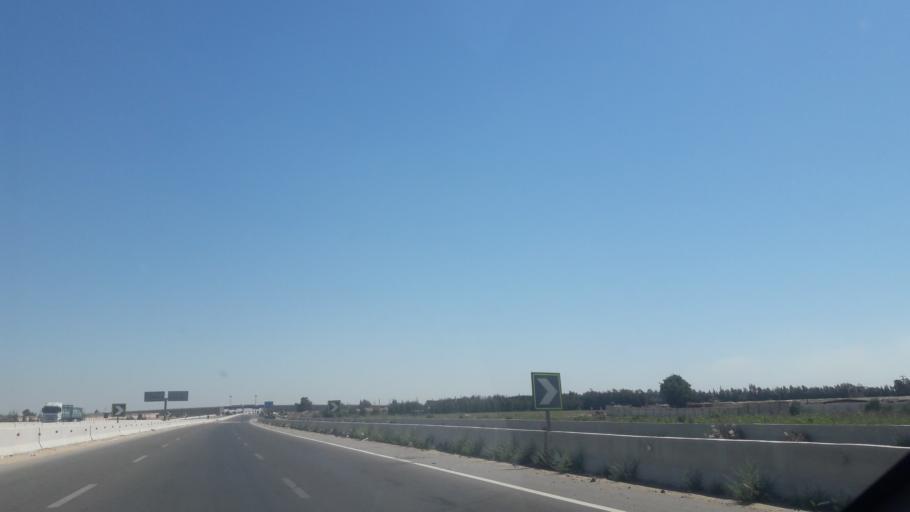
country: EG
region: Al Isma'iliyah
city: Ismailia
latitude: 30.8095
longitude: 32.1662
